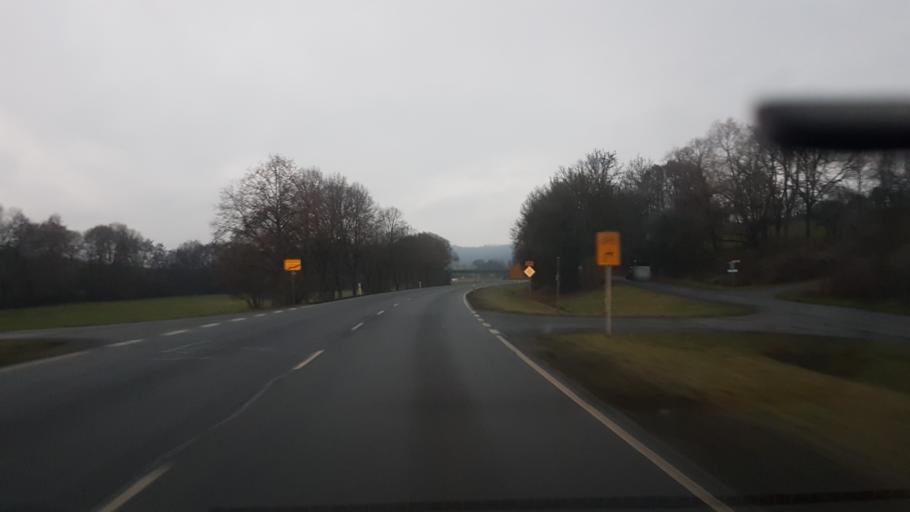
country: DE
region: Bavaria
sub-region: Regierungsbezirk Unterfranken
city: Pfarrweisach
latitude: 50.1722
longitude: 10.7140
